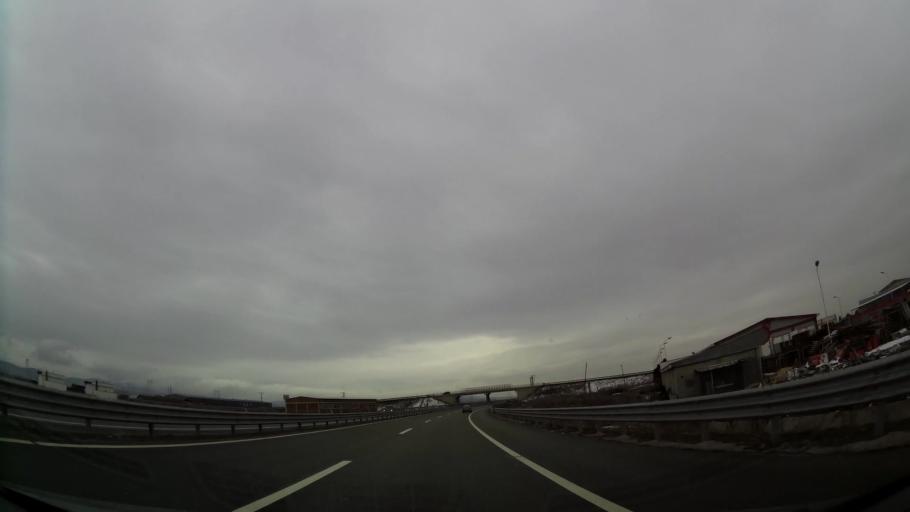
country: XK
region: Pristina
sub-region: Lipjan
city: Lipljan
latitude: 42.5278
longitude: 21.1650
